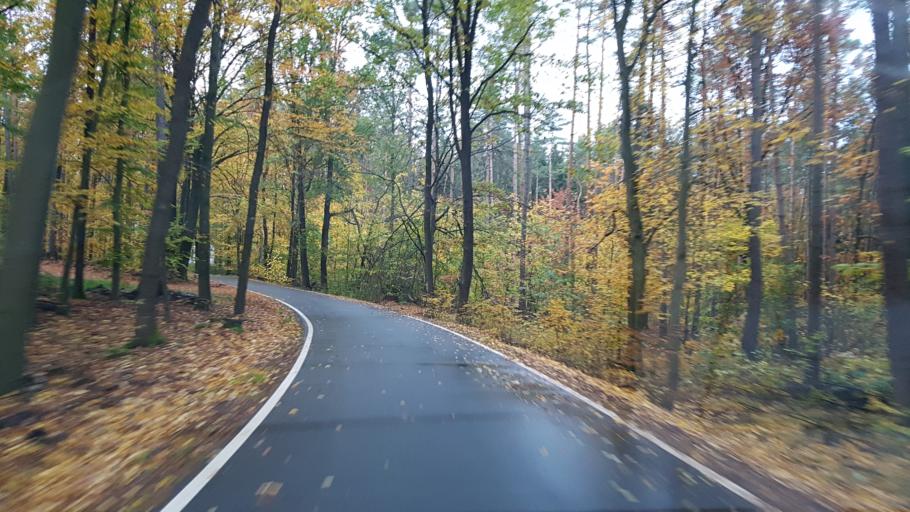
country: DE
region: Saxony
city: Cavertitz
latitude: 51.4181
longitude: 13.0759
